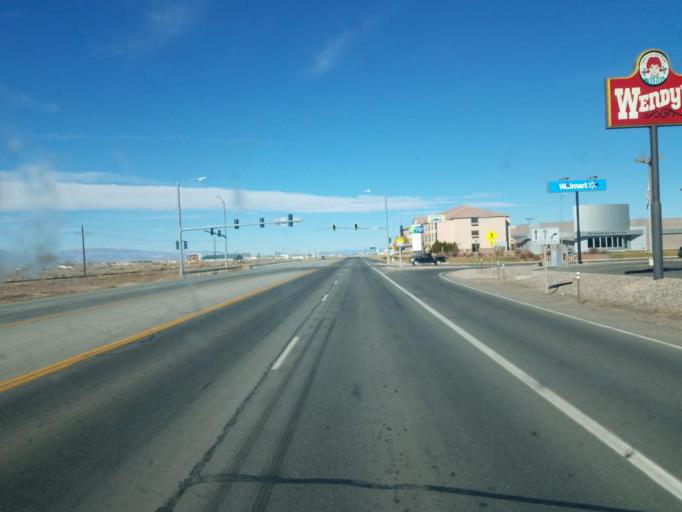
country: US
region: Colorado
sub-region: Alamosa County
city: Alamosa
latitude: 37.4798
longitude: -105.9054
